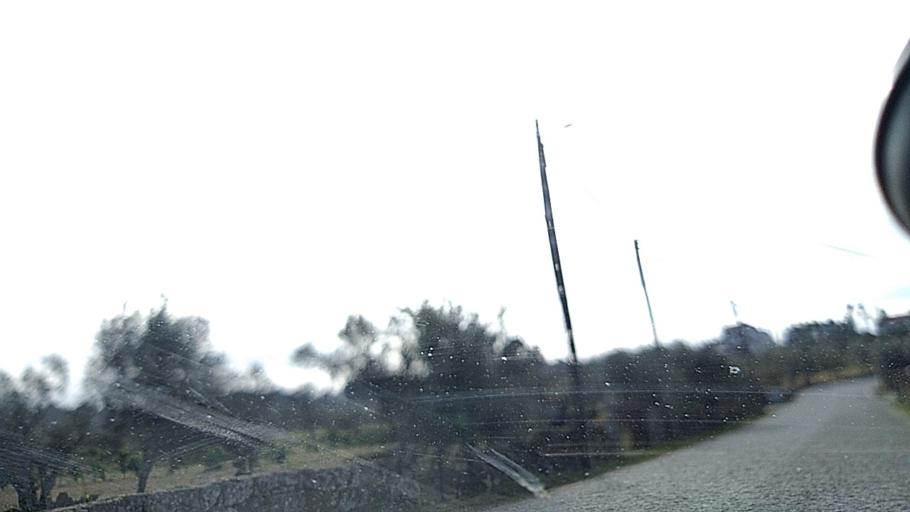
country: PT
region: Guarda
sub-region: Aguiar da Beira
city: Aguiar da Beira
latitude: 40.7637
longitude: -7.5408
